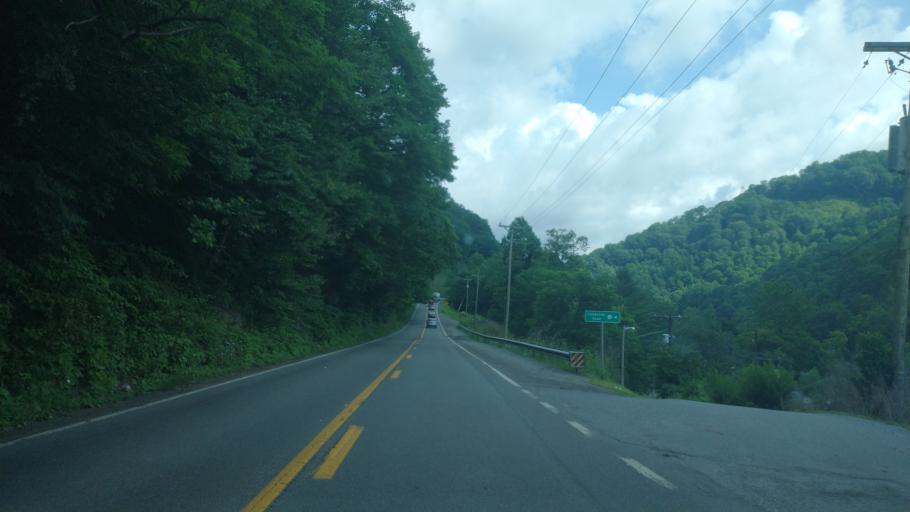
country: US
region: West Virginia
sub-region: McDowell County
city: Welch
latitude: 37.4079
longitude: -81.4261
